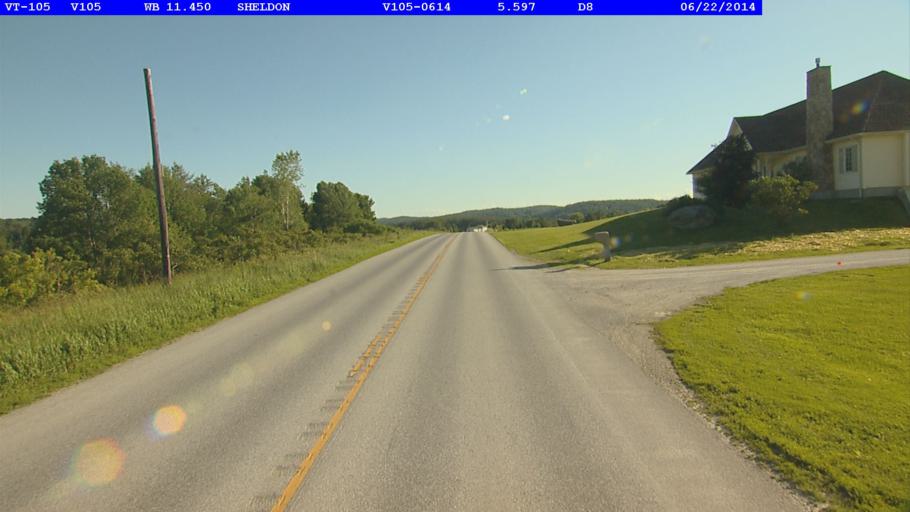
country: US
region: Vermont
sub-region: Franklin County
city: Enosburg Falls
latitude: 44.9053
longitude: -72.9255
